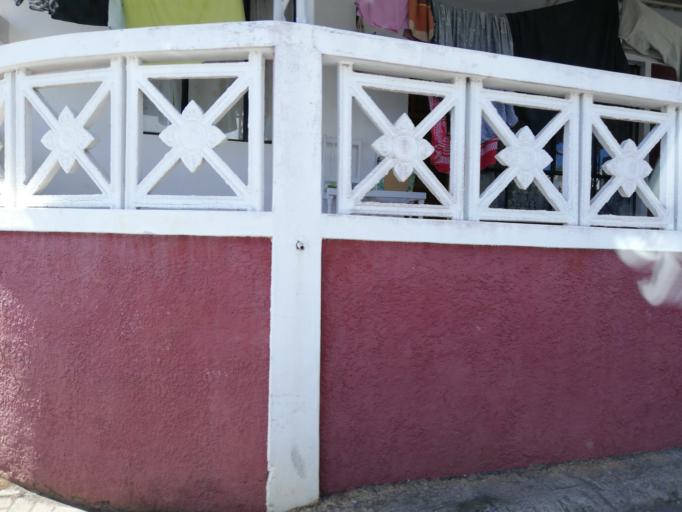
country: MU
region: Moka
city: Moka
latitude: -20.2300
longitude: 57.4981
